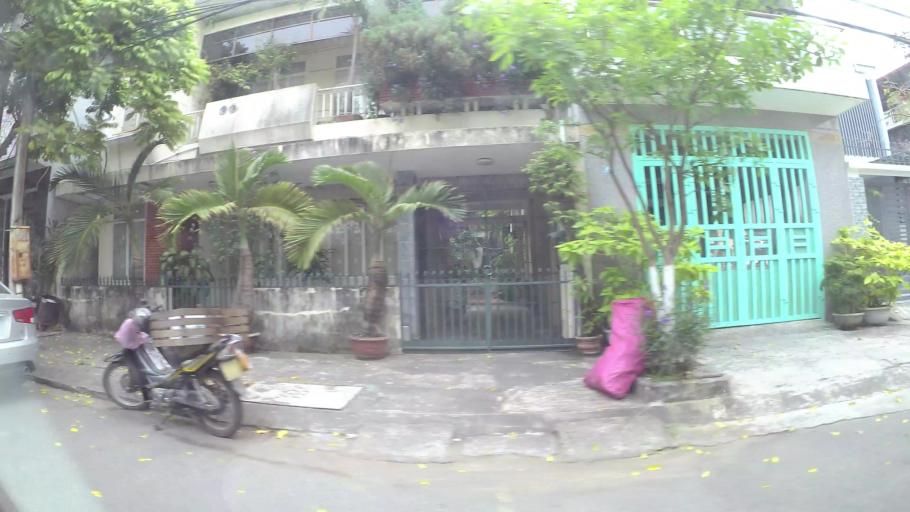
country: VN
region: Da Nang
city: Da Nang
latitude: 16.0818
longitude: 108.2148
